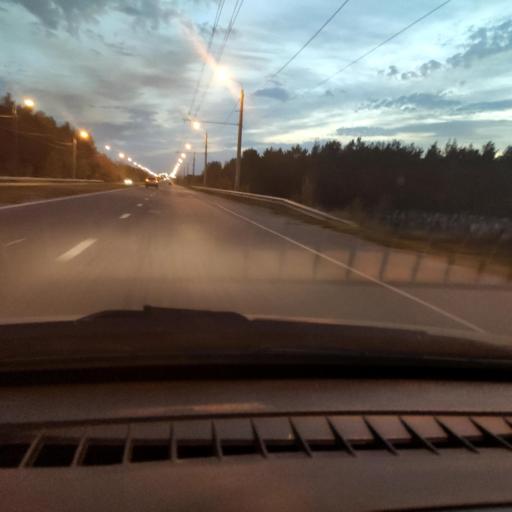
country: RU
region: Samara
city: Zhigulevsk
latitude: 53.5273
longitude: 49.5491
